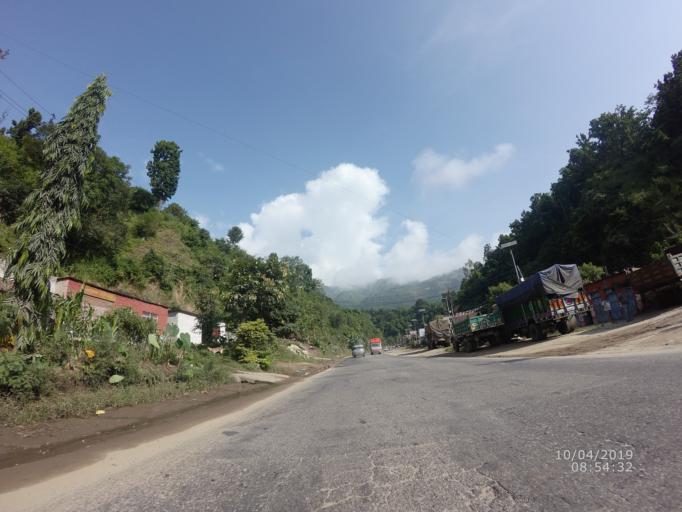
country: NP
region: Central Region
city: Kirtipur
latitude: 27.7977
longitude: 84.9943
